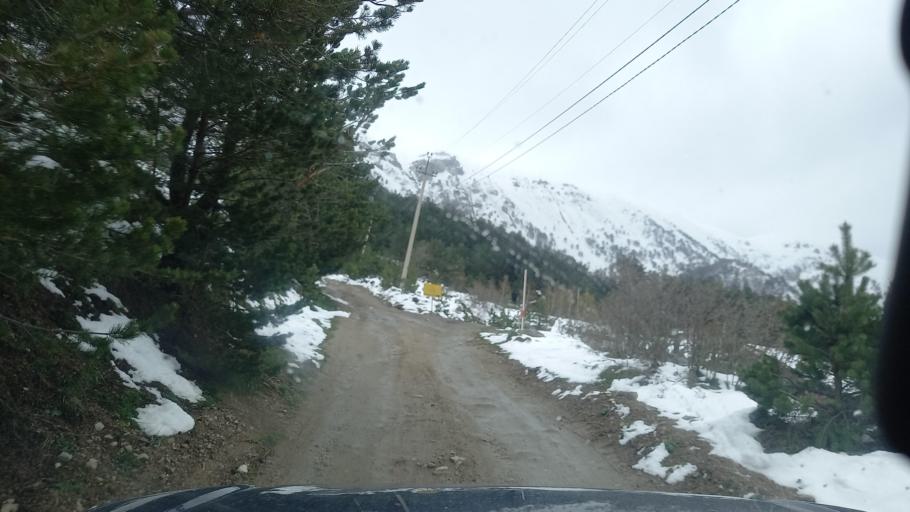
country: RU
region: North Ossetia
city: Mizur
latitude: 42.8079
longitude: 43.9582
